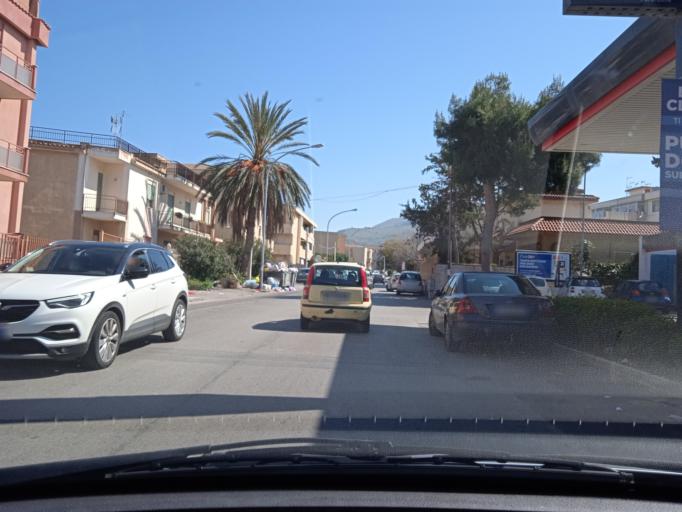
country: IT
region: Sicily
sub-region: Palermo
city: Villabate
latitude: 38.0916
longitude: 13.4316
